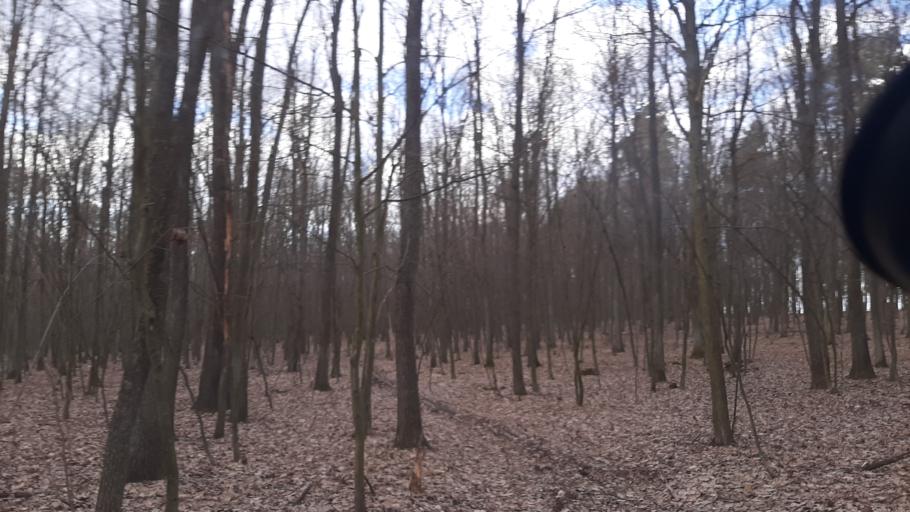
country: PL
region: Lublin Voivodeship
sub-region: Powiat lubelski
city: Jastkow
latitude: 51.3713
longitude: 22.4147
